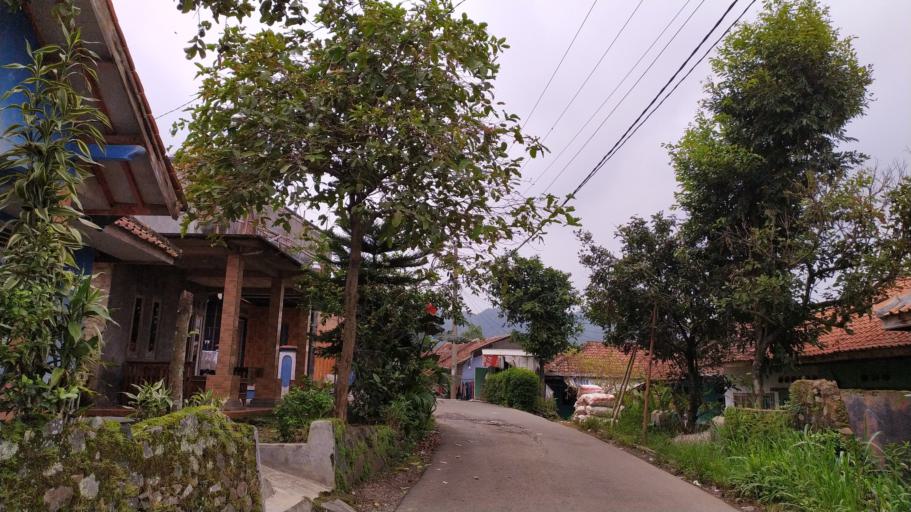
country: ID
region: West Java
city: Ciampea
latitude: -6.6155
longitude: 106.7087
